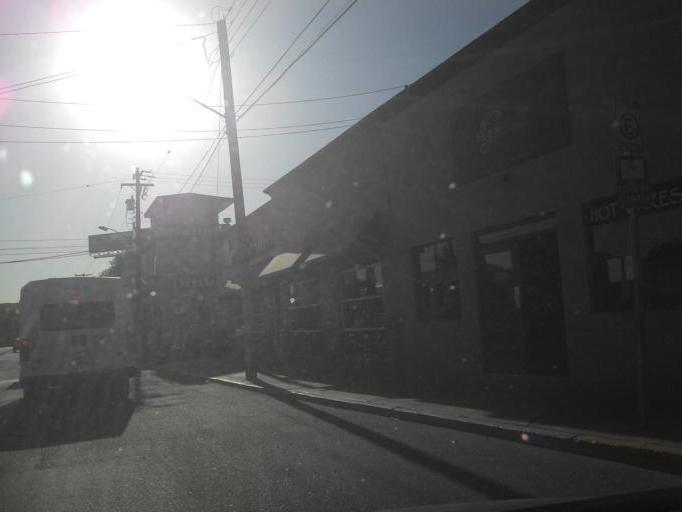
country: MX
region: Baja California
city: Tijuana
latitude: 32.5251
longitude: -117.0249
